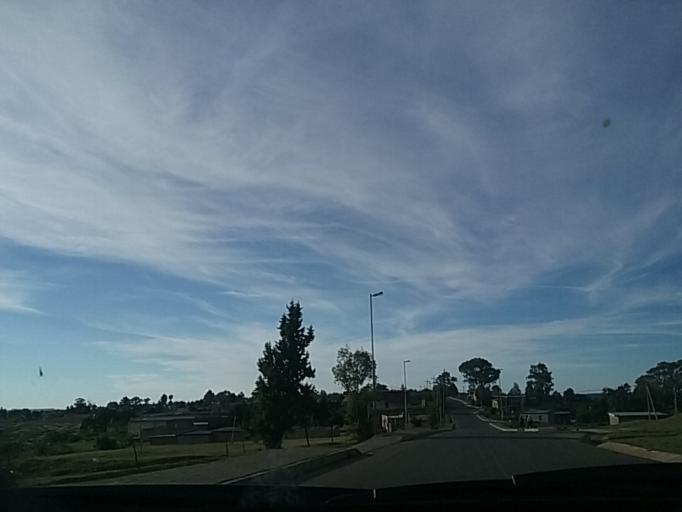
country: LS
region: Berea
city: Teyateyaneng
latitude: -29.1438
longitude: 27.7385
